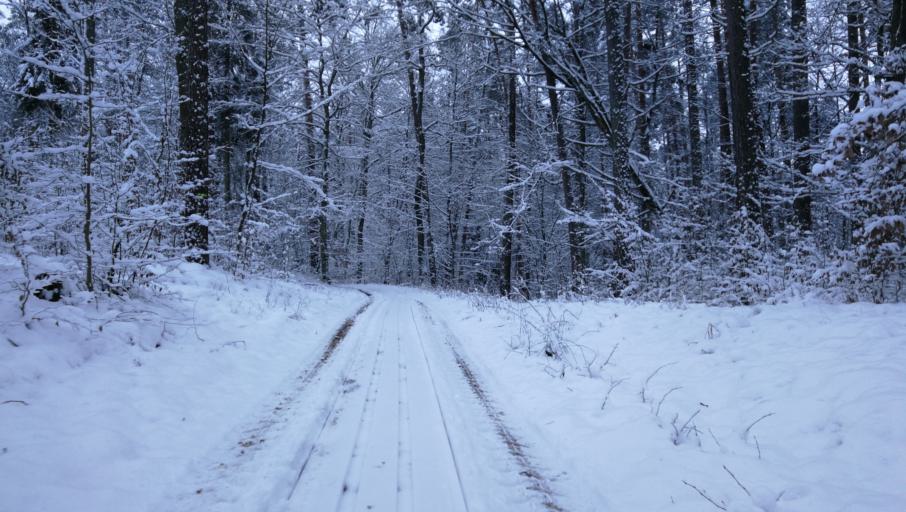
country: PL
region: Kujawsko-Pomorskie
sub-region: Powiat brodnicki
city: Gorzno
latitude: 53.2052
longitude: 19.6971
